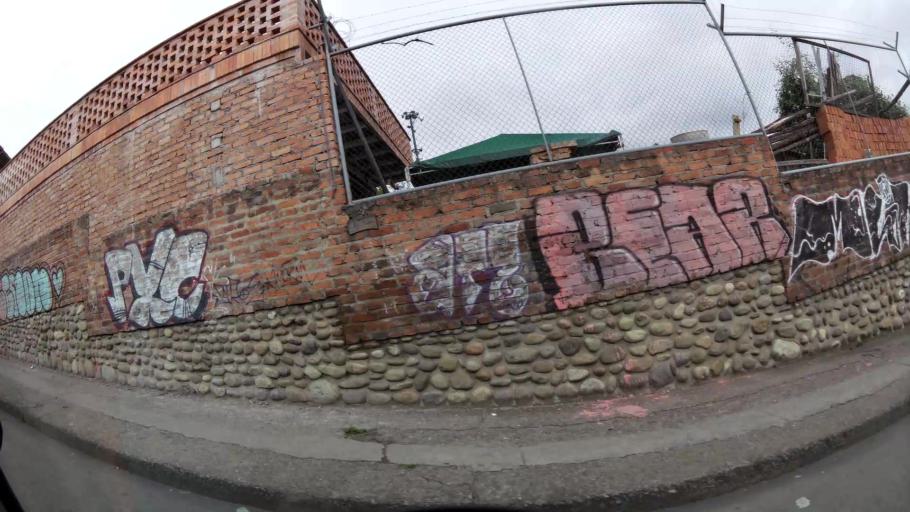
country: EC
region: Azuay
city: Cuenca
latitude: -2.8985
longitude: -78.9903
